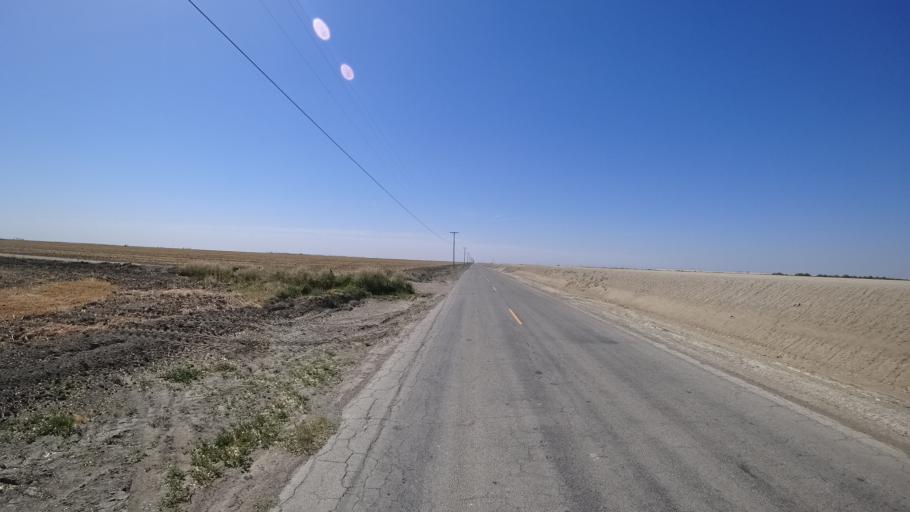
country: US
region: California
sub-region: Kings County
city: Corcoran
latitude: 36.0148
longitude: -119.5361
